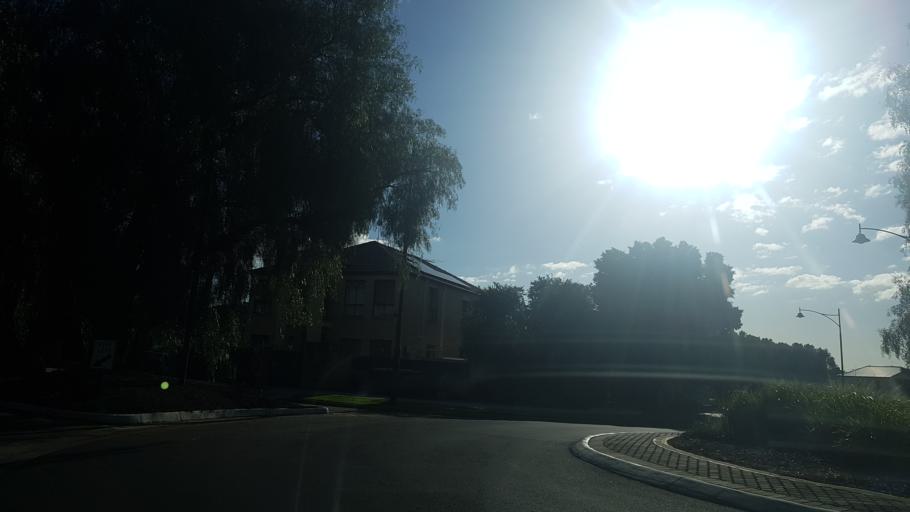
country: AU
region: South Australia
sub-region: Salisbury
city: Ingle Farm
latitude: -34.8226
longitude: 138.6122
